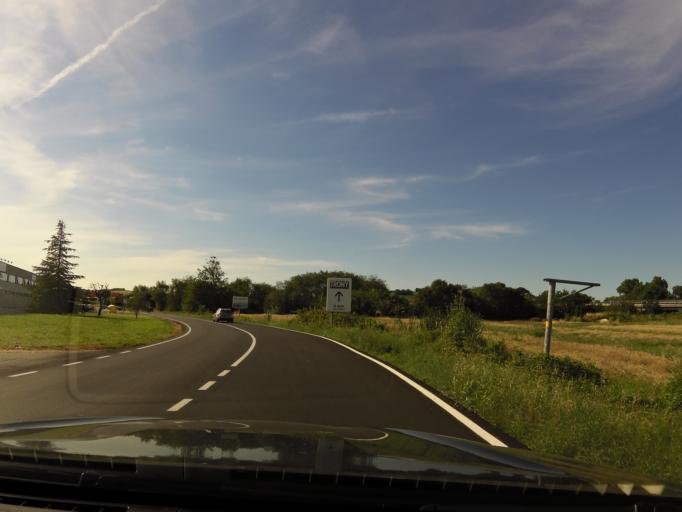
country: IT
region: The Marches
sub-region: Provincia di Ancona
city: Camerano
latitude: 43.5229
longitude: 13.5270
